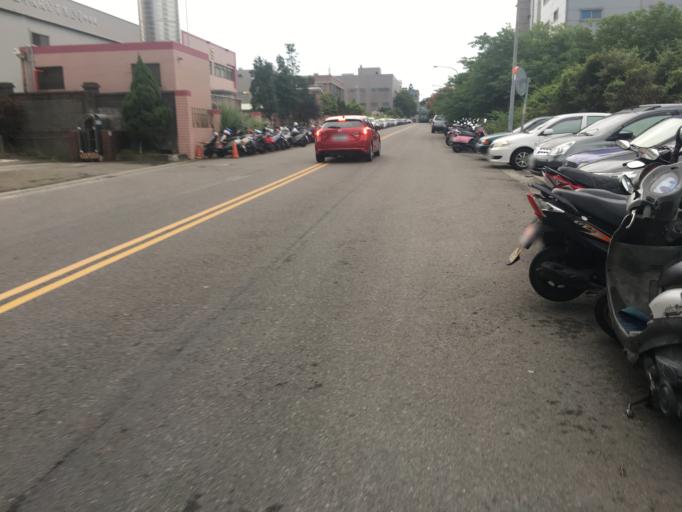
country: TW
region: Taiwan
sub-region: Hsinchu
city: Hsinchu
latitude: 24.7258
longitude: 120.9103
